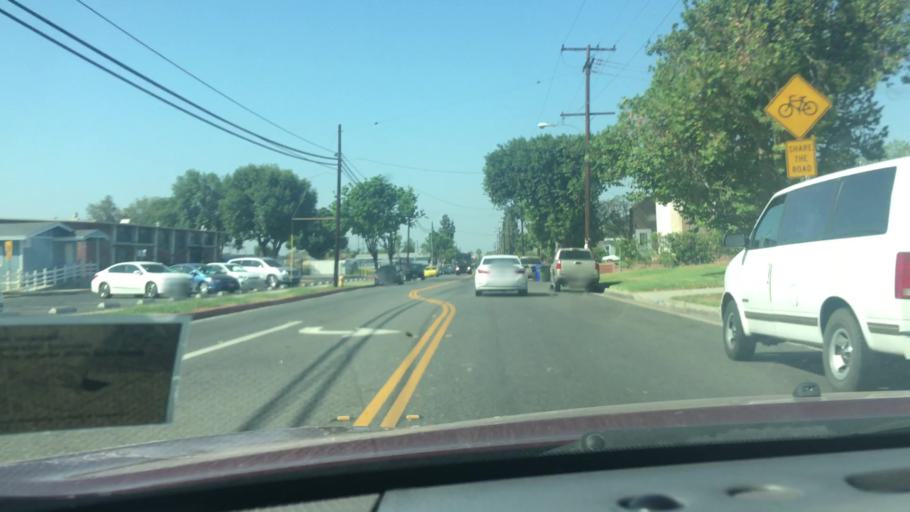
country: US
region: California
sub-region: Los Angeles County
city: La Mirada
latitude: 33.9299
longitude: -118.0209
